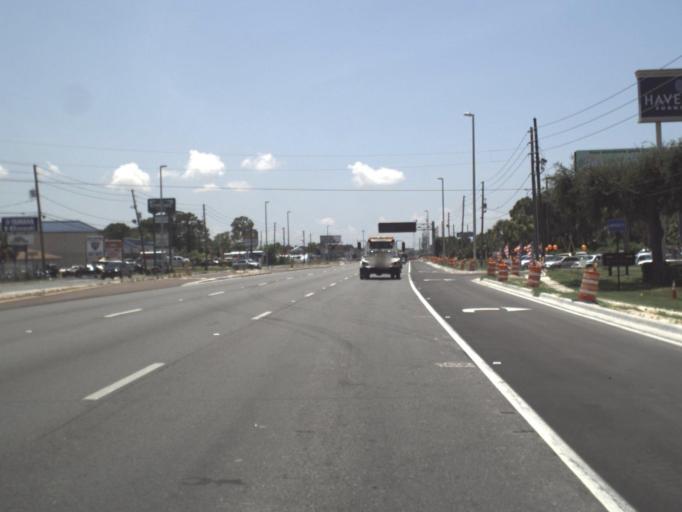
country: US
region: Florida
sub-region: Pasco County
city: Port Richey
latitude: 28.2866
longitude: -82.7137
